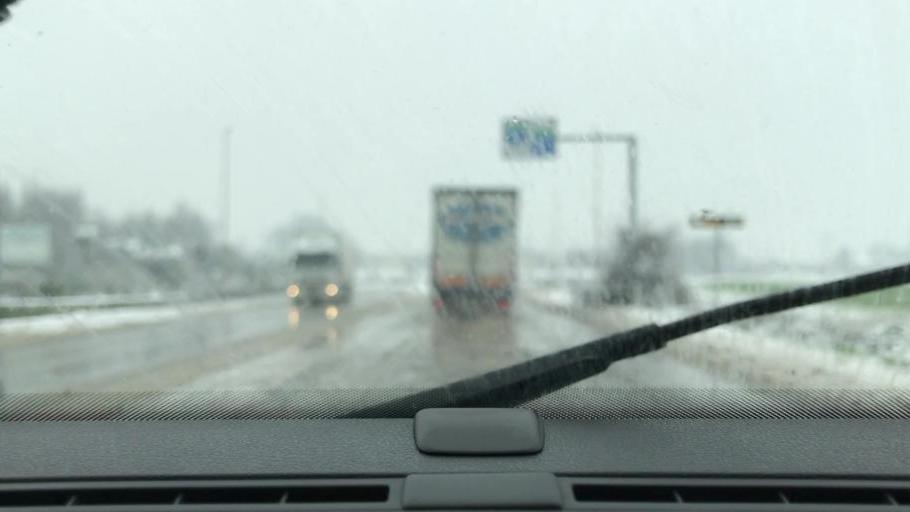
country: IT
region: Lombardy
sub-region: Provincia di Mantova
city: Goito
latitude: 45.2552
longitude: 10.6649
